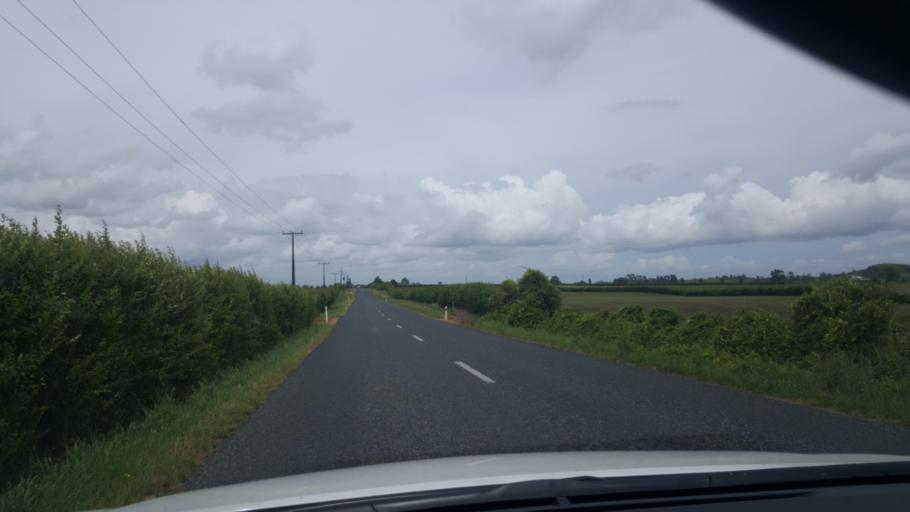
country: NZ
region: Waikato
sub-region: Matamata-Piako District
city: Matamata
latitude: -37.8760
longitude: 175.7267
